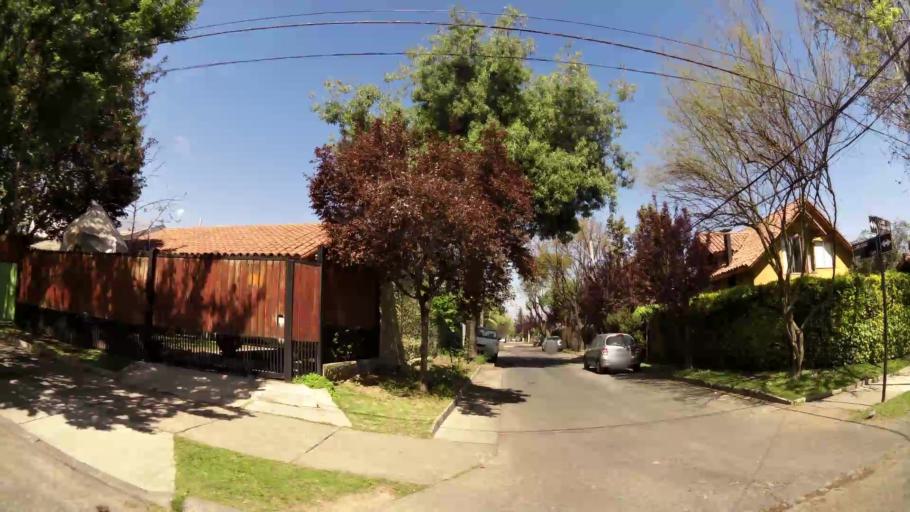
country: CL
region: Santiago Metropolitan
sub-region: Provincia de Santiago
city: Villa Presidente Frei, Nunoa, Santiago, Chile
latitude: -33.4212
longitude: -70.5457
